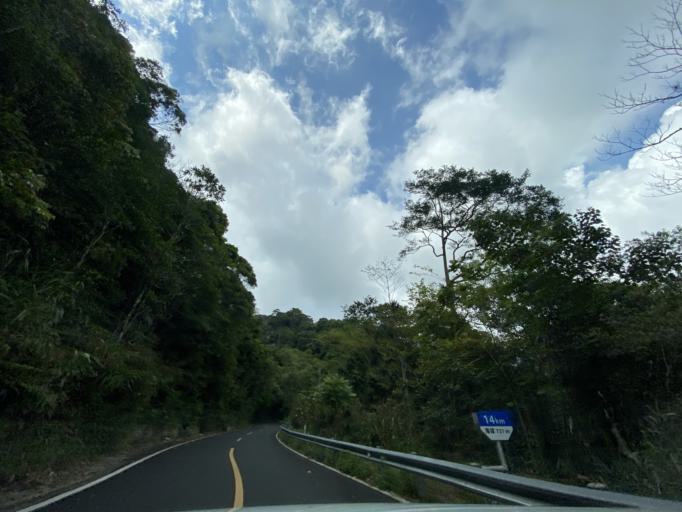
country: CN
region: Hainan
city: Diaoluoshan
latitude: 18.7038
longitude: 109.8825
